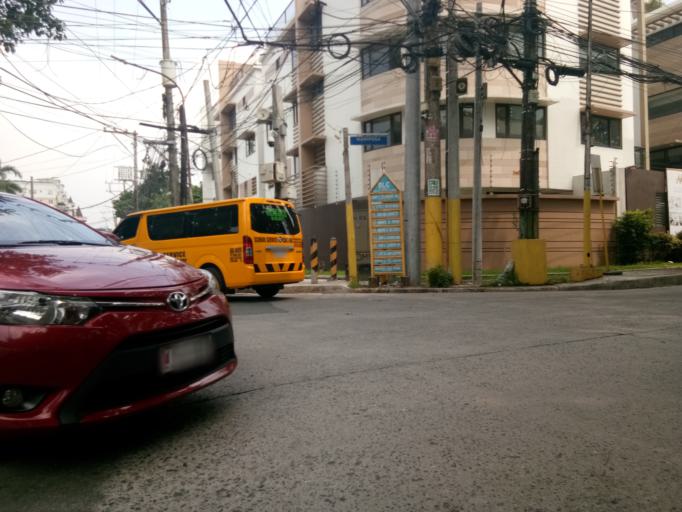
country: PH
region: Metro Manila
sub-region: San Juan
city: San Juan
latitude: 14.6125
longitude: 121.0460
